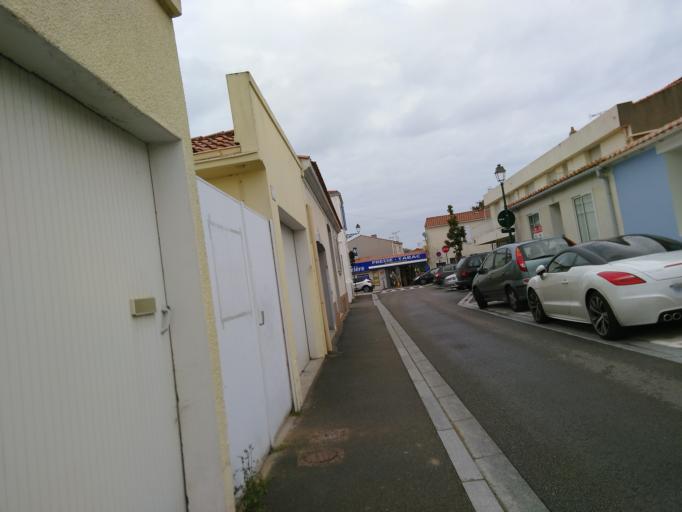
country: FR
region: Pays de la Loire
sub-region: Departement de la Vendee
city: Les Sables-d'Olonne
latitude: 46.4958
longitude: -1.8011
